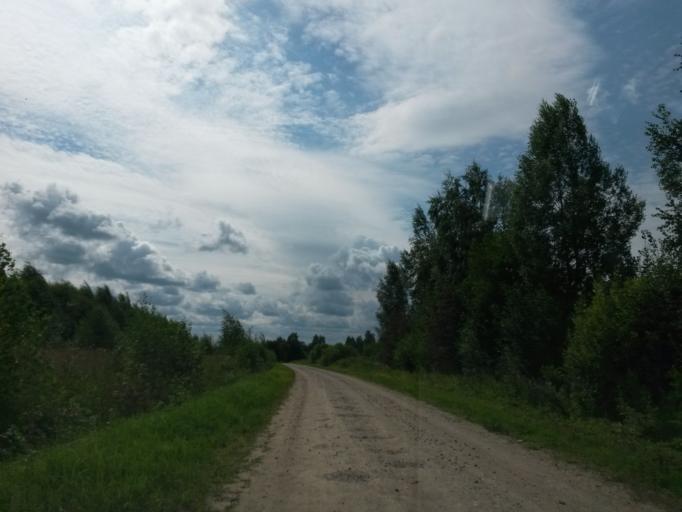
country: RU
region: Jaroslavl
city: Tutayev
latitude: 57.9413
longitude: 39.4465
